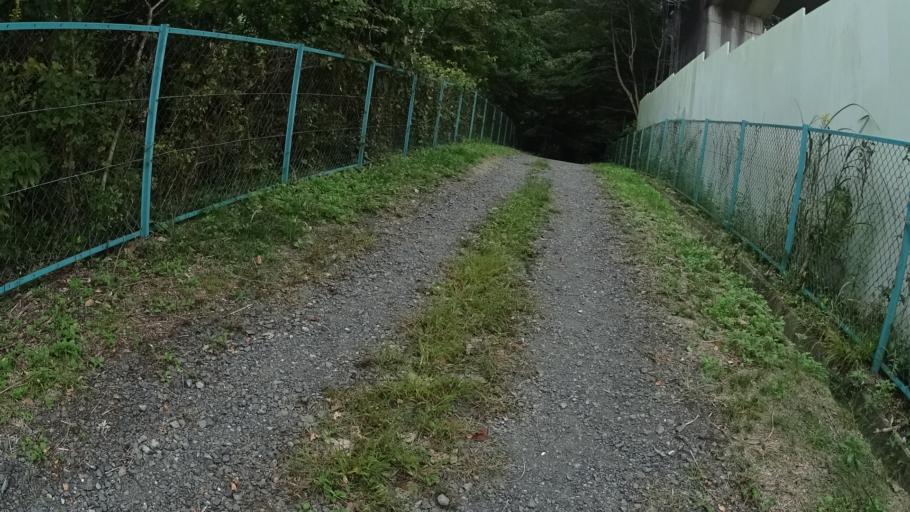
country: JP
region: Kanagawa
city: Zushi
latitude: 35.3507
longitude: 139.5947
